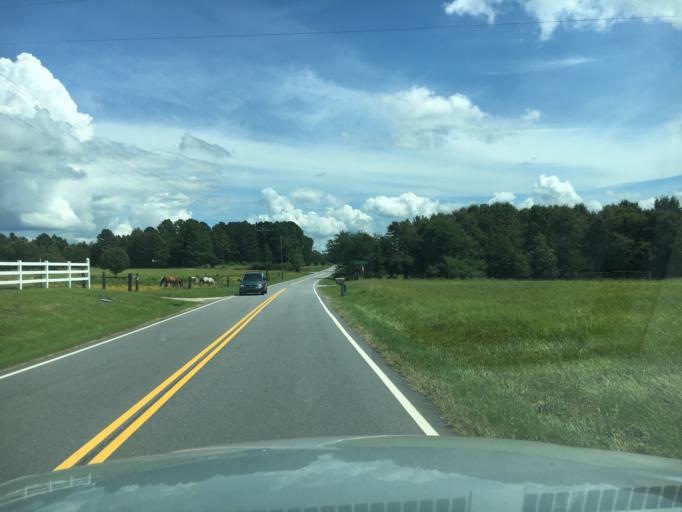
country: US
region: South Carolina
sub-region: Anderson County
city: Belton
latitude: 34.5192
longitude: -82.4229
